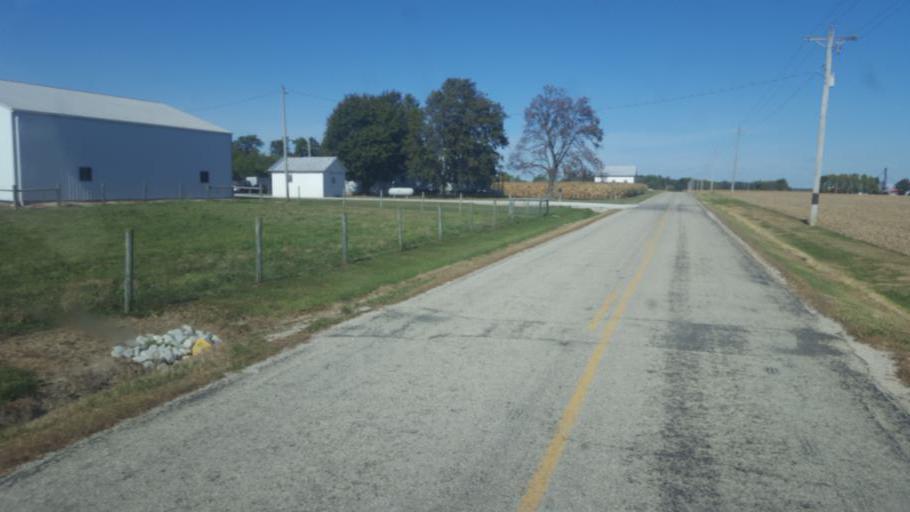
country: US
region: Ohio
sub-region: Huron County
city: Willard
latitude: 40.9755
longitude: -82.7908
